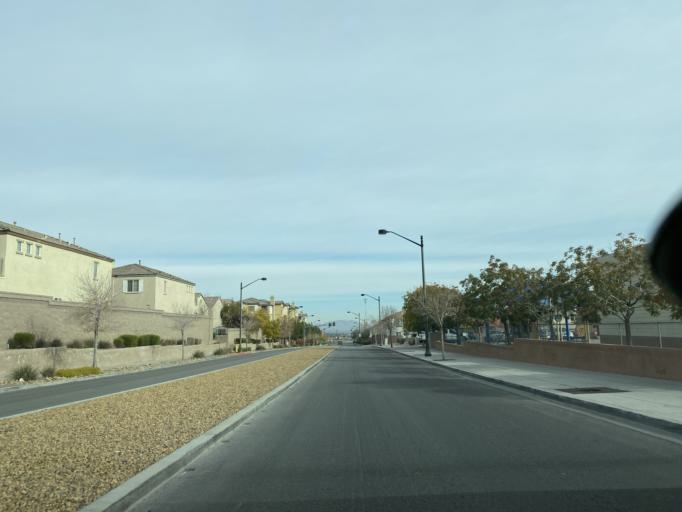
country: US
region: Nevada
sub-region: Clark County
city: Summerlin South
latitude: 36.2955
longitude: -115.2937
